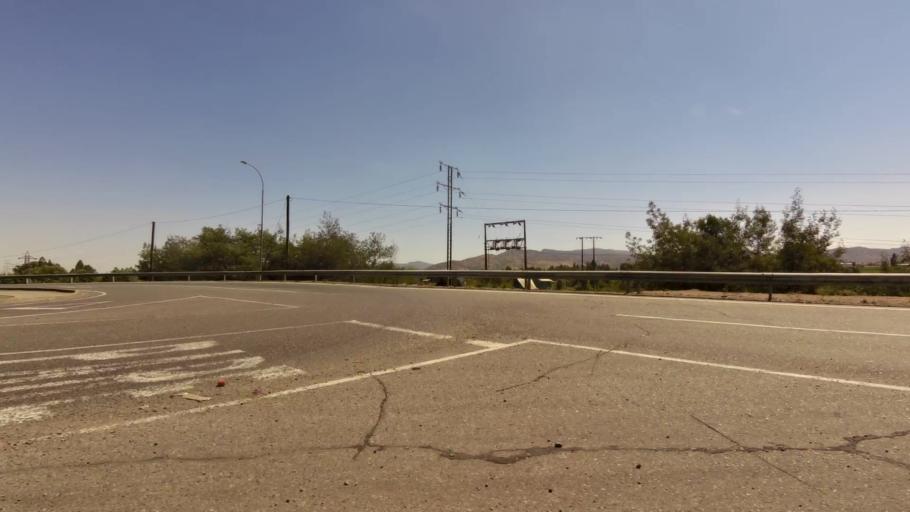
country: CL
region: Maule
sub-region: Provincia de Talca
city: Talca
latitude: -35.3024
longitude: -71.5191
